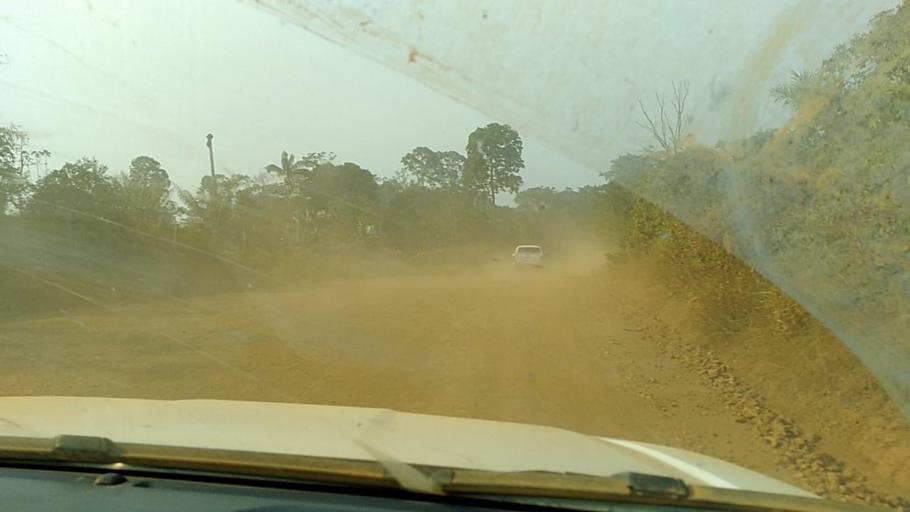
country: BR
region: Rondonia
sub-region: Porto Velho
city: Porto Velho
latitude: -8.7485
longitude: -63.9643
